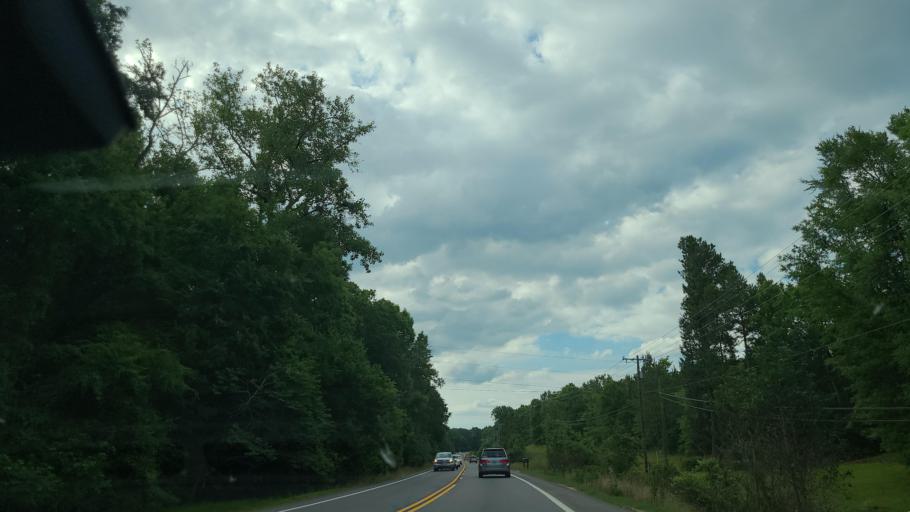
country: US
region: Georgia
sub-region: Putnam County
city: Eatonton
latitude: 33.2284
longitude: -83.4318
